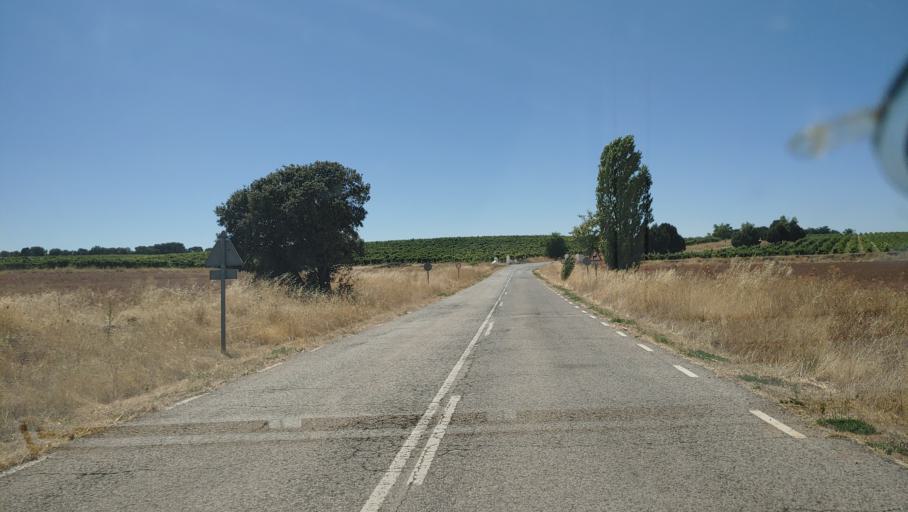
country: ES
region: Castille-La Mancha
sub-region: Provincia de Albacete
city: Ossa de Montiel
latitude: 38.8976
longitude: -2.7632
